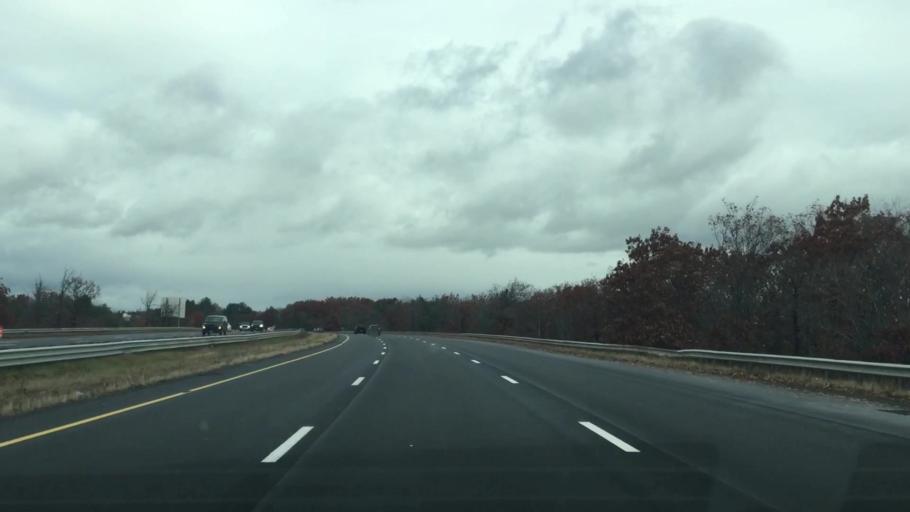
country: US
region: Massachusetts
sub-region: Essex County
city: Methuen
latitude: 42.7327
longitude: -71.2034
